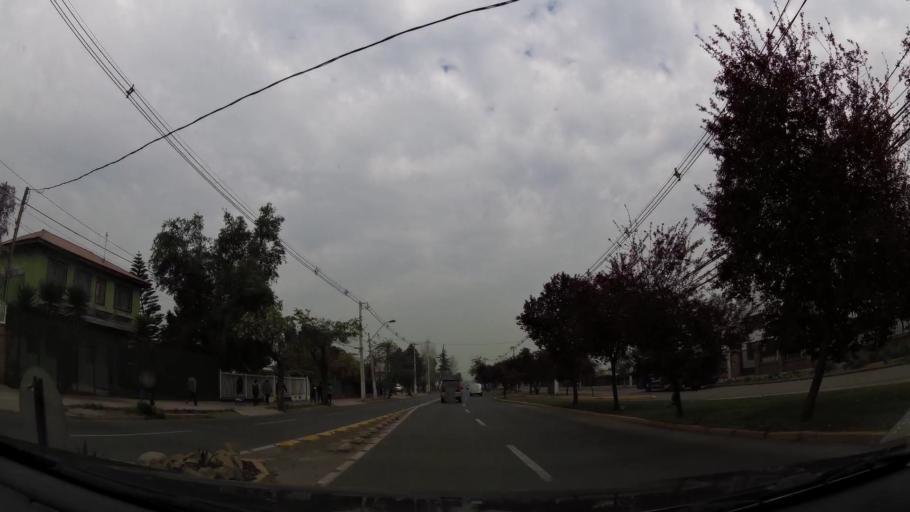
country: CL
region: Santiago Metropolitan
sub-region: Provincia de Chacabuco
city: Chicureo Abajo
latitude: -33.2082
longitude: -70.6789
